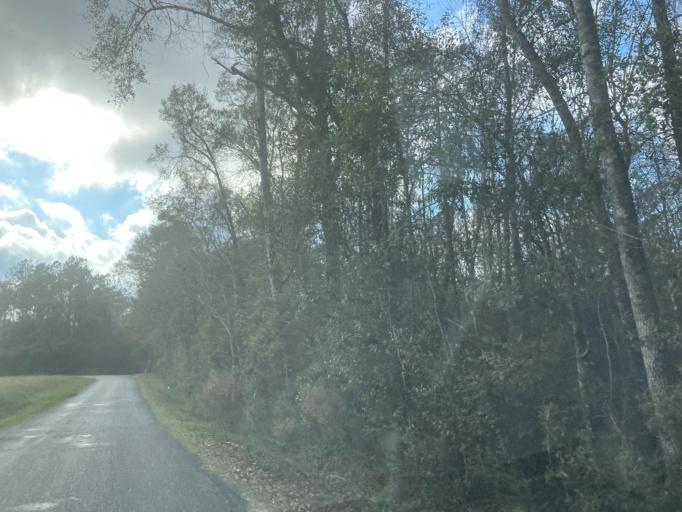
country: US
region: Mississippi
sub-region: Stone County
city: Wiggins
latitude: 30.8005
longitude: -89.1077
